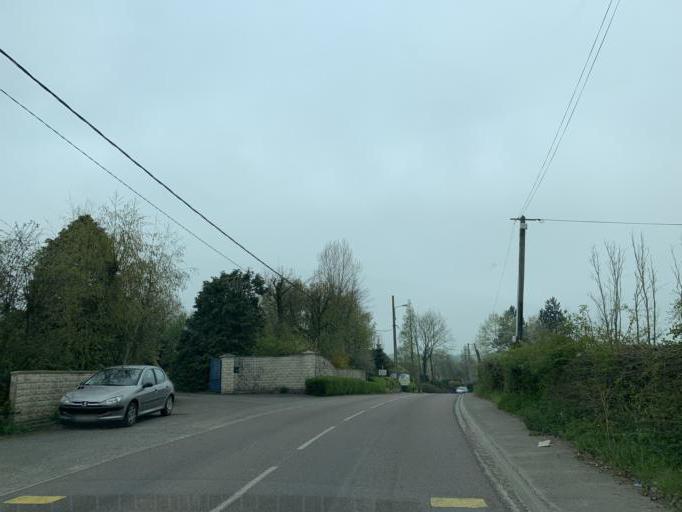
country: FR
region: Nord-Pas-de-Calais
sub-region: Departement du Pas-de-Calais
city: Rinxent
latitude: 50.7805
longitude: 1.7340
